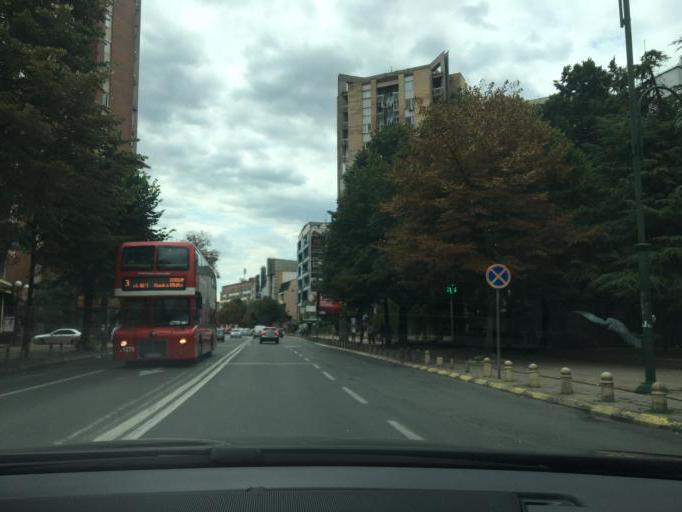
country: MK
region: Karpos
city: Skopje
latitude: 41.9952
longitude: 21.4278
